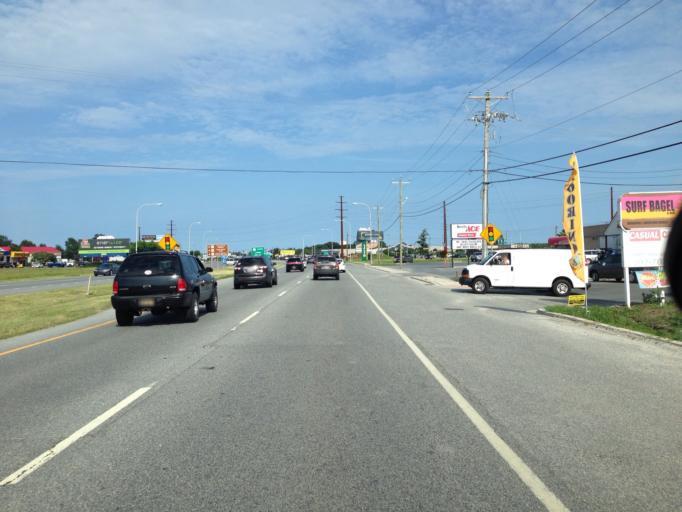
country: US
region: Delaware
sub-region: Sussex County
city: Lewes
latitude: 38.7489
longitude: -75.1782
